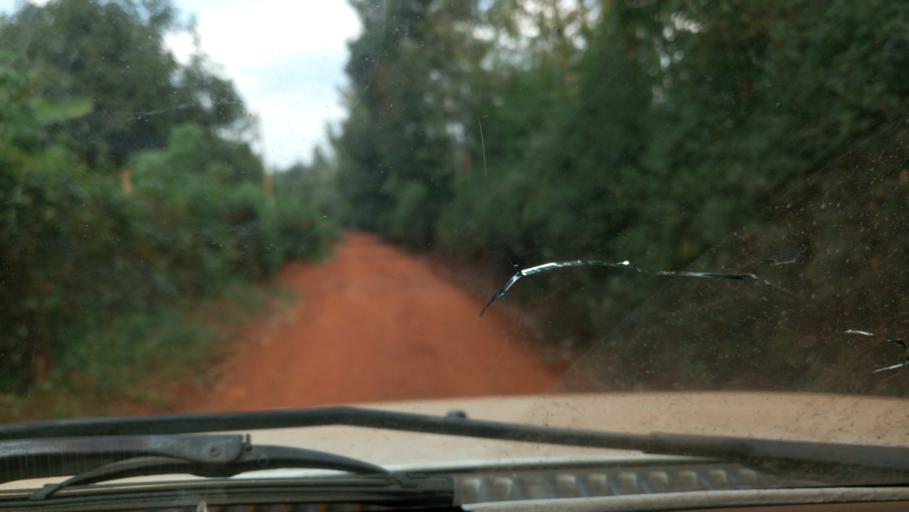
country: KE
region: Nairobi Area
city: Thika
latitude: -0.9240
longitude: 36.9813
